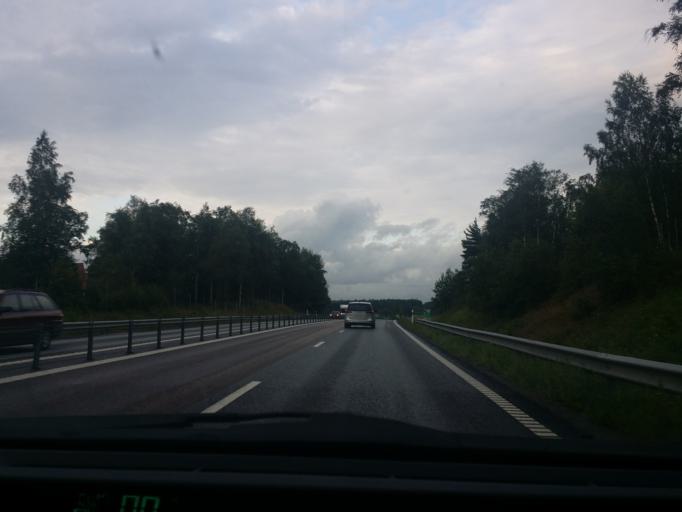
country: SE
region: Vaestmanland
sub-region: Kopings Kommun
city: Koping
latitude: 59.5321
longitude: 15.9852
